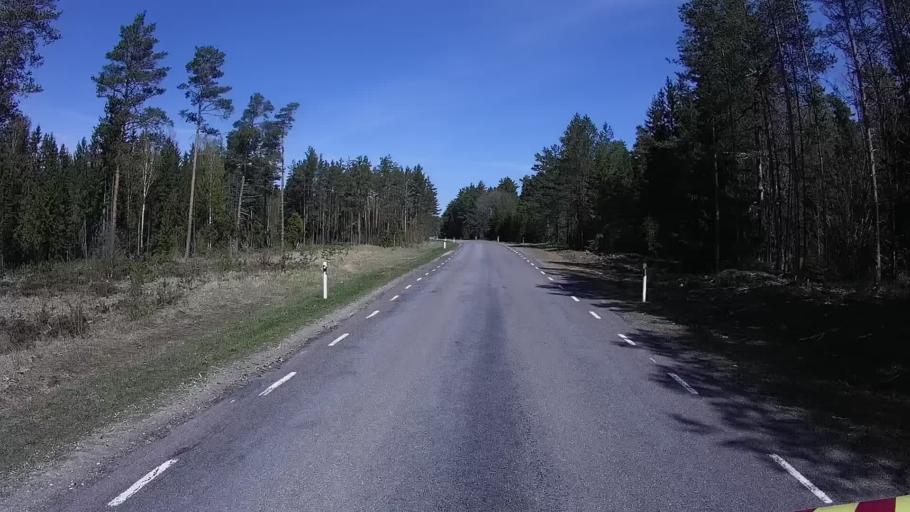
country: EE
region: Harju
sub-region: Nissi vald
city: Turba
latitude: 59.1231
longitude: 24.0637
